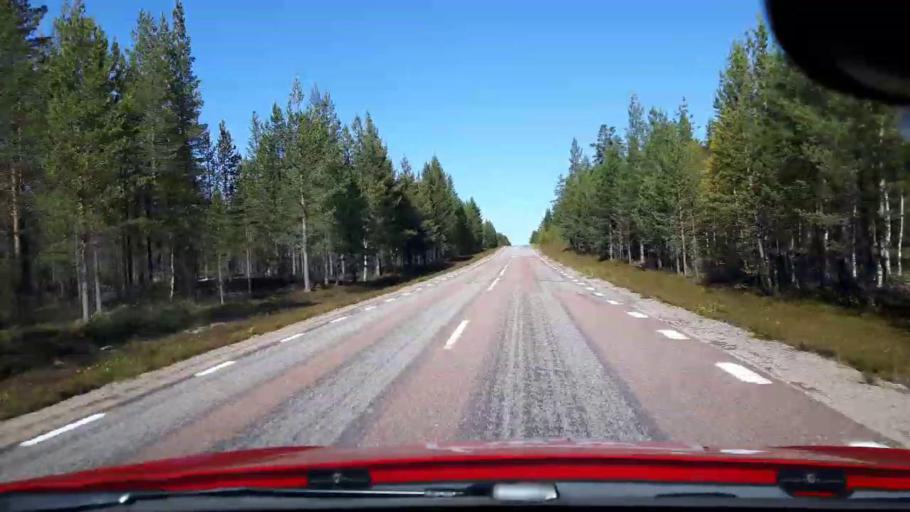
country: SE
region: Jaemtland
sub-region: Harjedalens Kommun
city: Sveg
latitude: 61.7219
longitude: 14.1675
